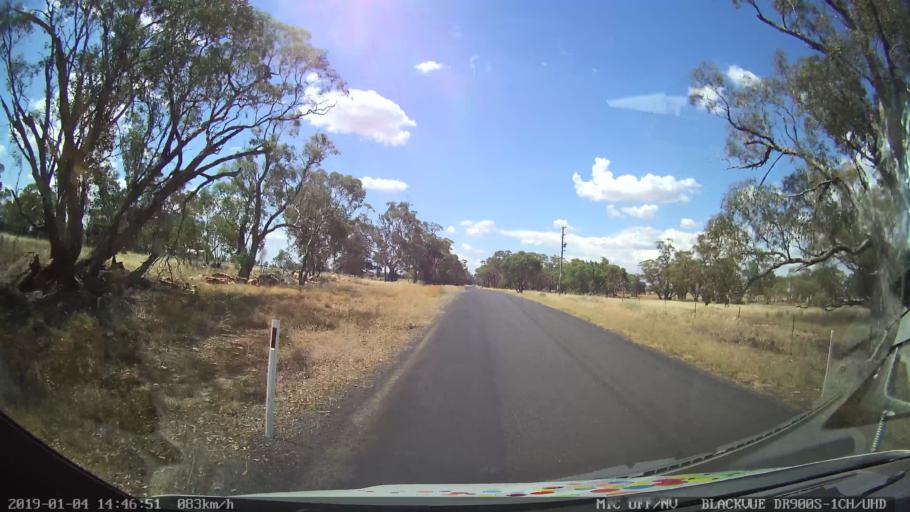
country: AU
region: New South Wales
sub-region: Dubbo Municipality
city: Dubbo
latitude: -32.0763
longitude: 148.6591
